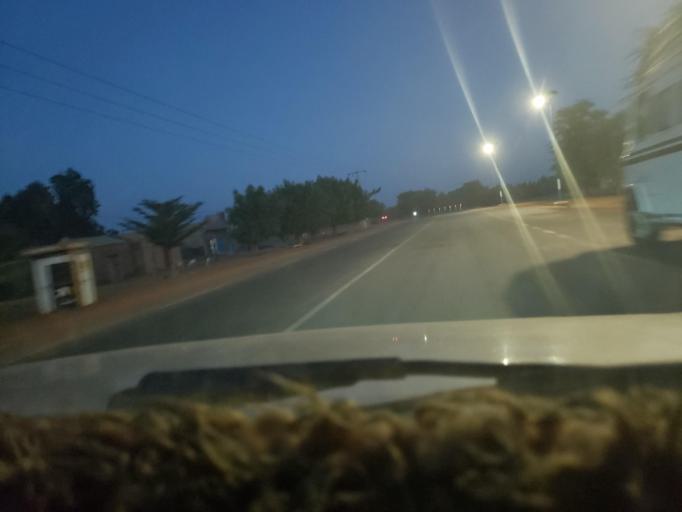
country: SN
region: Louga
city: Ndibene Dahra
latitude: 15.3847
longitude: -15.2365
